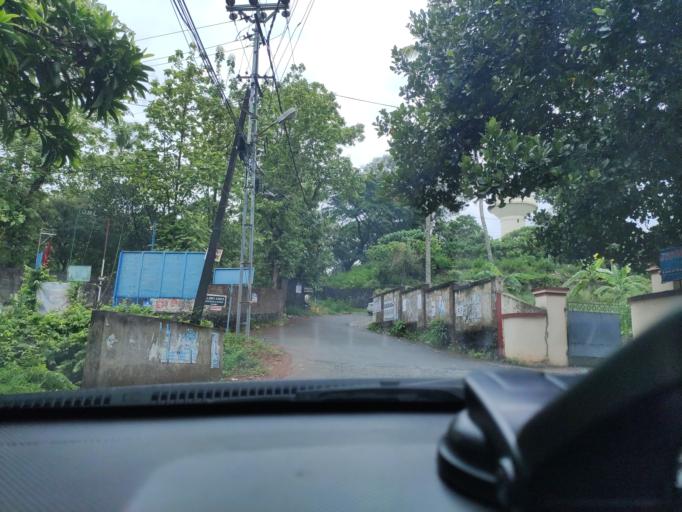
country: IN
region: Kerala
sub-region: Ernakulam
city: Elur
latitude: 10.0274
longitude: 76.3317
